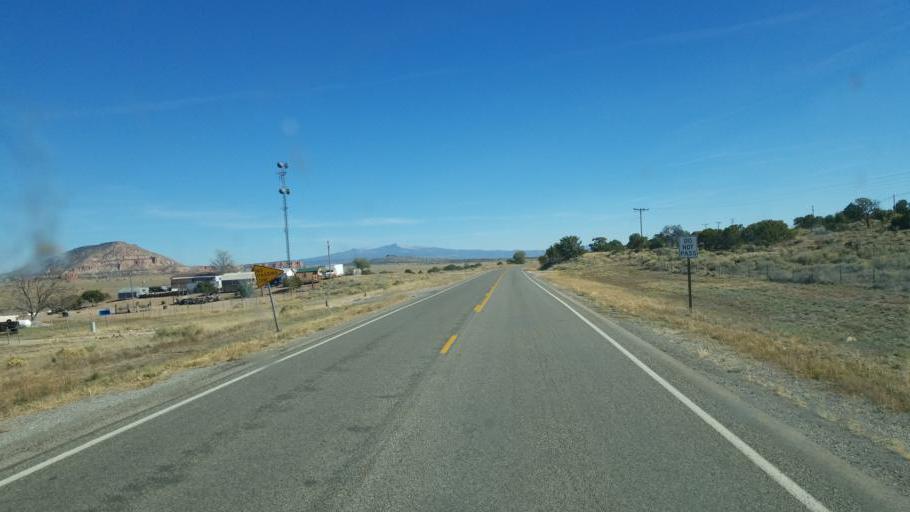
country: US
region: New Mexico
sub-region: McKinley County
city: Thoreau
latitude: 35.3552
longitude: -108.0213
